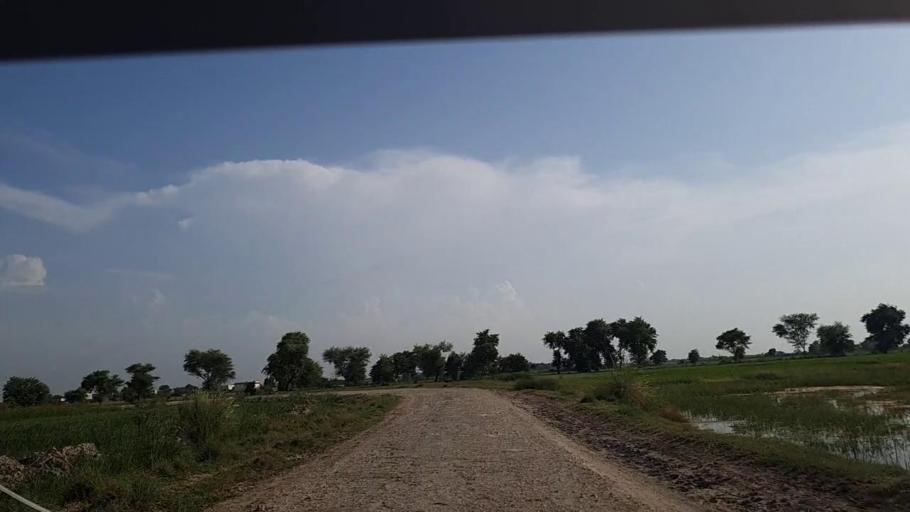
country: PK
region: Sindh
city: Khanpur
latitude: 27.8432
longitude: 69.3756
